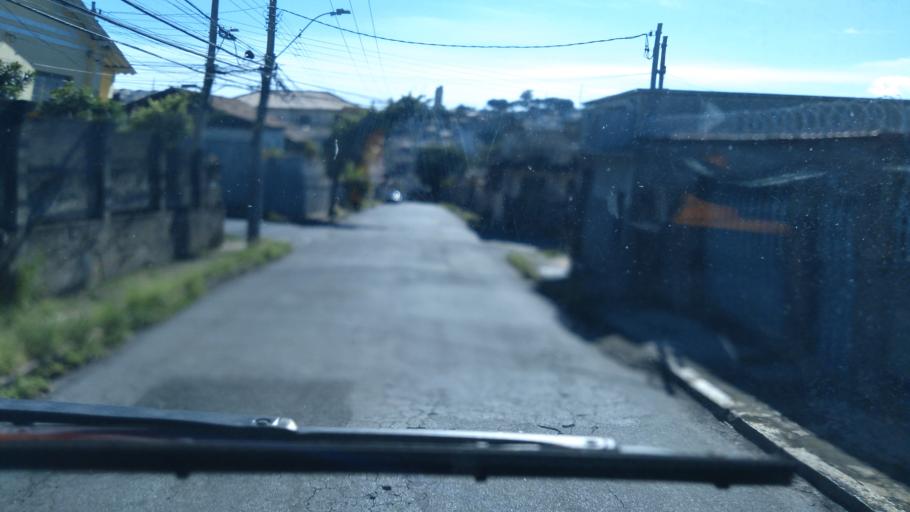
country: BR
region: Minas Gerais
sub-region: Belo Horizonte
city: Belo Horizonte
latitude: -19.9050
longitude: -43.9589
